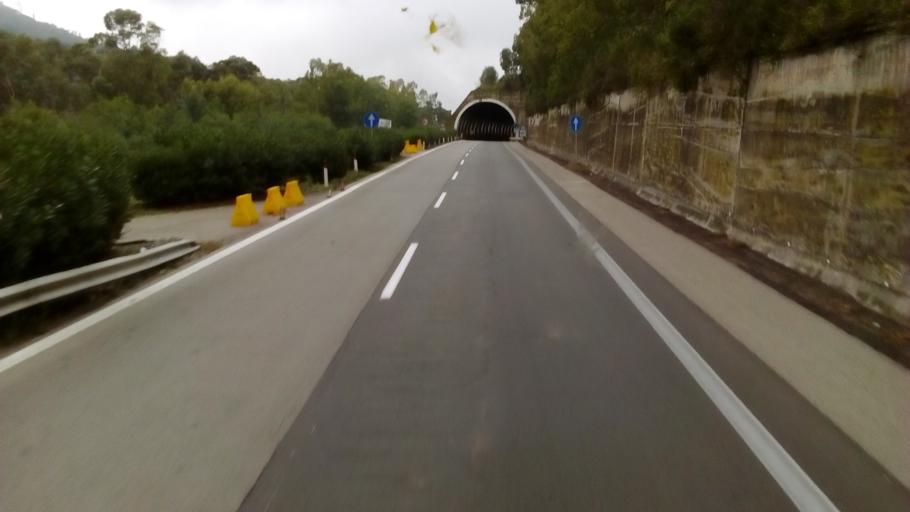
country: IT
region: Sicily
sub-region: Enna
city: Calascibetta
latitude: 37.5803
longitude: 14.2839
